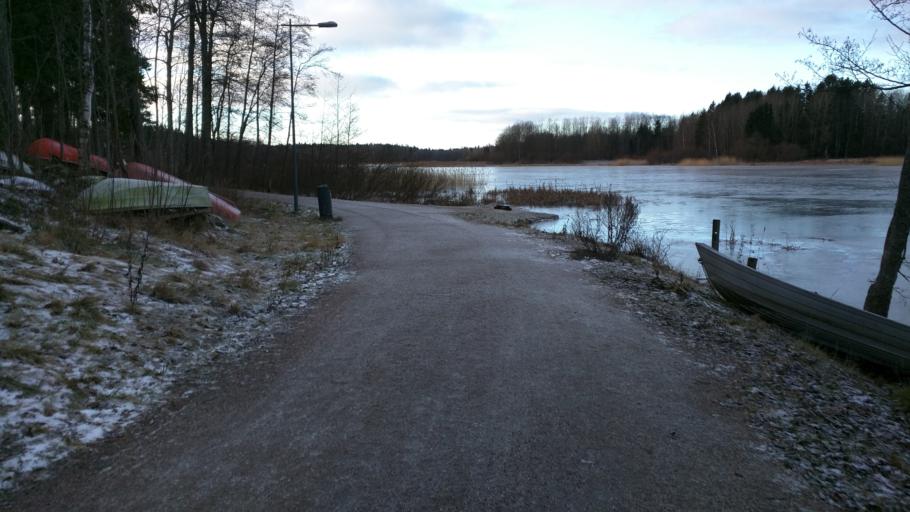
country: FI
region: Uusimaa
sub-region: Helsinki
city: Kauniainen
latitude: 60.2452
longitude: 24.7354
